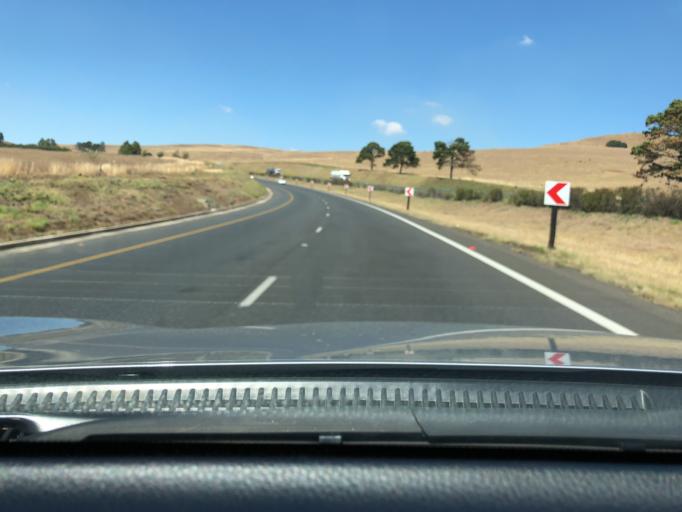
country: ZA
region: KwaZulu-Natal
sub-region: uMgungundlovu District Municipality
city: Mooirivier
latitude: -29.1051
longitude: 29.9394
